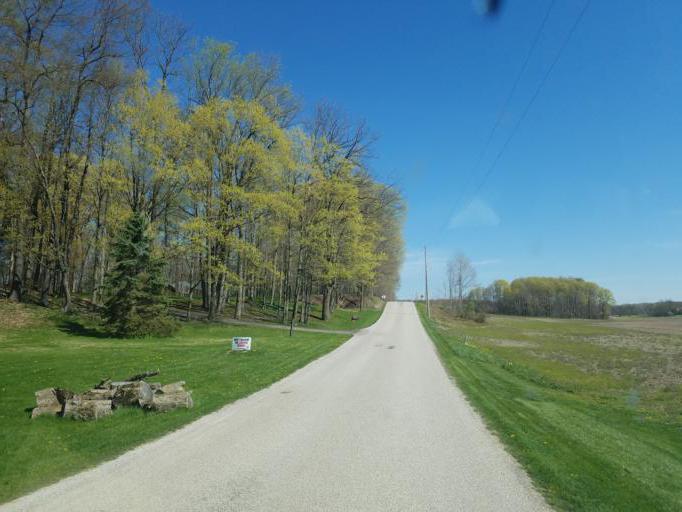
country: US
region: Ohio
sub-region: Morrow County
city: Mount Gilead
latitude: 40.5686
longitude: -82.7961
